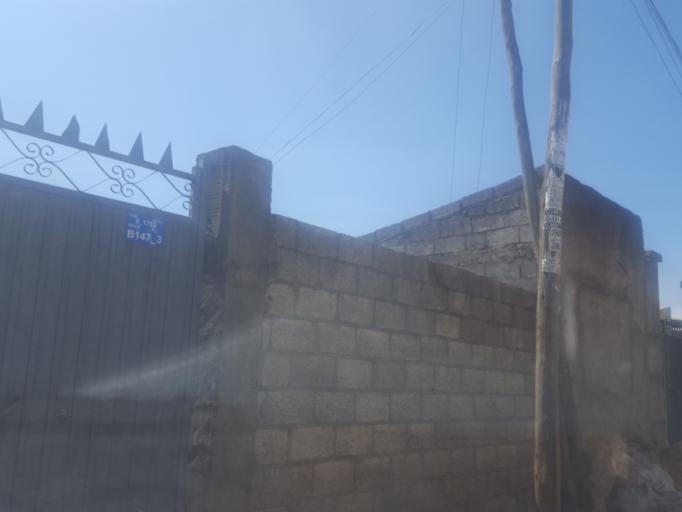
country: ET
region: Adis Abeba
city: Addis Ababa
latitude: 9.0695
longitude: 38.7323
